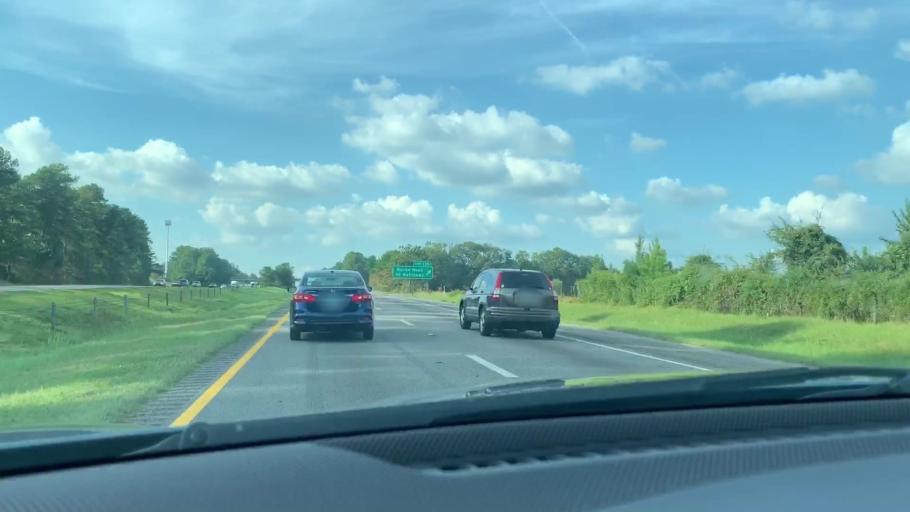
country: US
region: South Carolina
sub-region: Calhoun County
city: Saint Matthews
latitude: 33.6295
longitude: -80.8733
